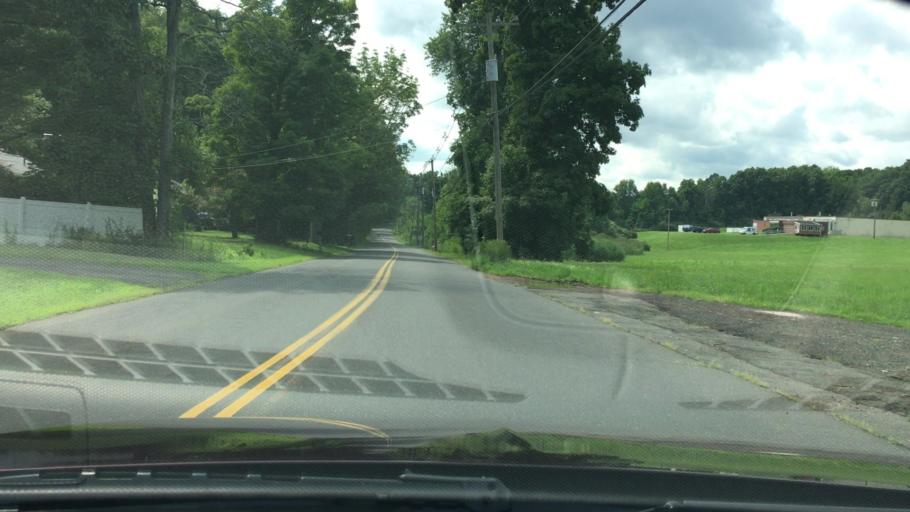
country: US
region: Connecticut
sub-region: Hartford County
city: Kensington
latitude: 41.6138
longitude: -72.7652
